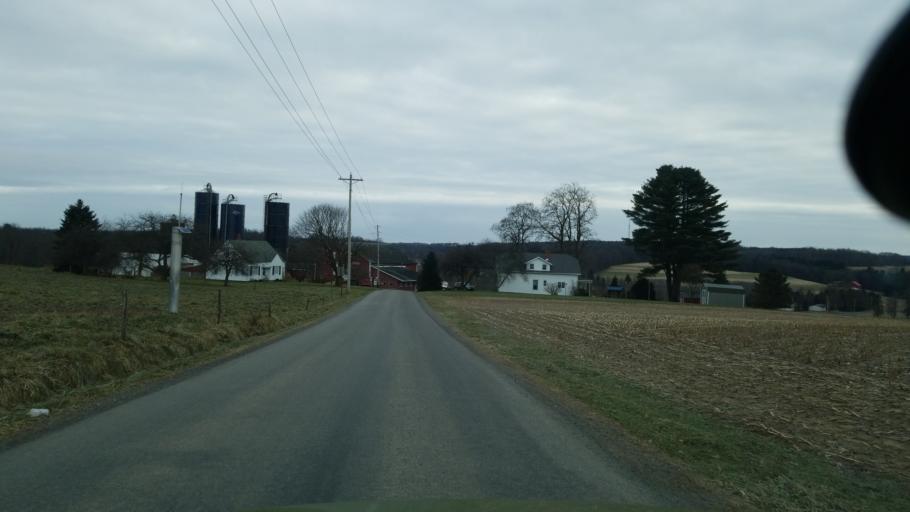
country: US
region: Pennsylvania
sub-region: Clearfield County
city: Treasure Lake
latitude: 41.1097
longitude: -78.6614
